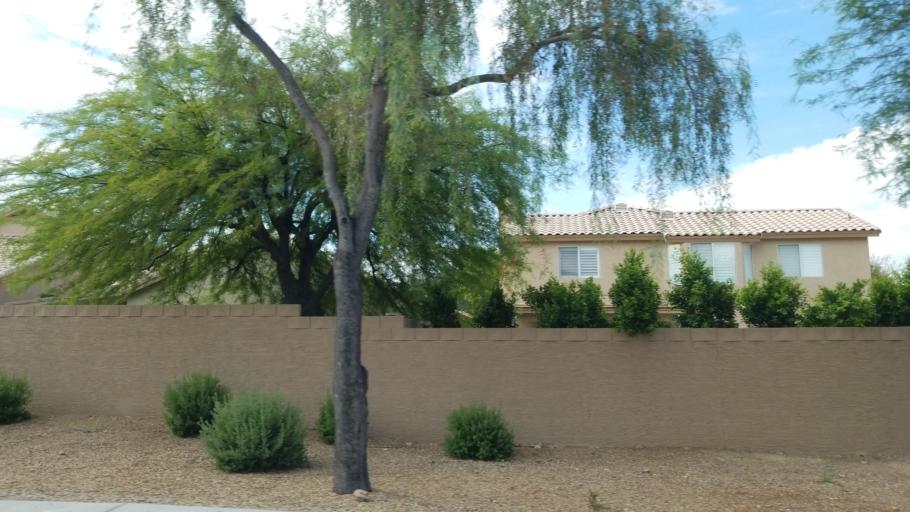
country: US
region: Arizona
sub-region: Maricopa County
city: Paradise Valley
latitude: 33.6149
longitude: -112.0547
